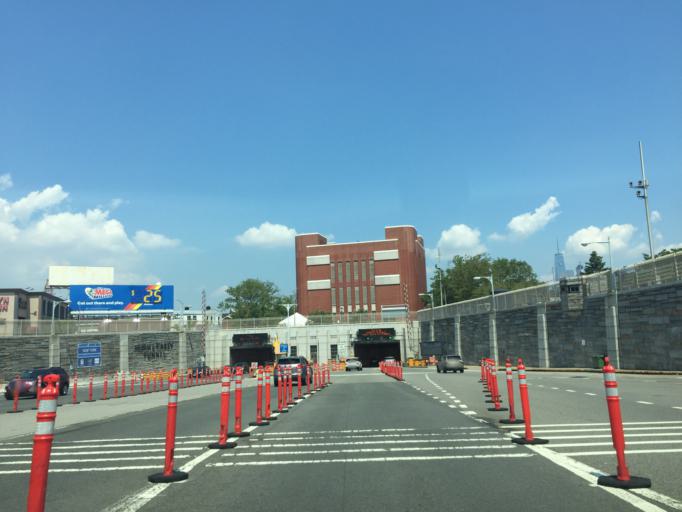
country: US
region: New York
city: New York City
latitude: 40.6811
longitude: -74.0049
